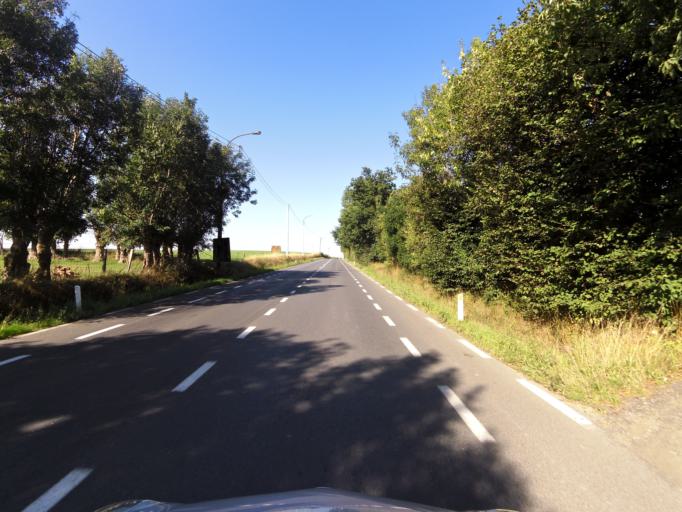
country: BE
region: Flanders
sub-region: Provincie Oost-Vlaanderen
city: Oudenaarde
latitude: 50.8311
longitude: 3.6531
